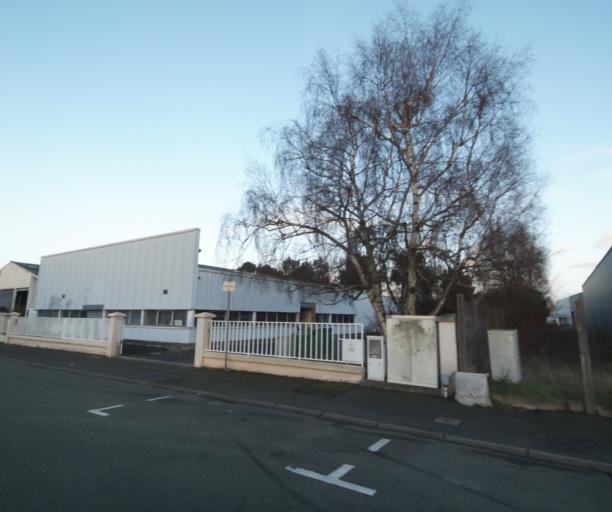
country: FR
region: Pays de la Loire
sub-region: Departement de la Sarthe
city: Le Mans
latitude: 47.9624
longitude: 0.2139
